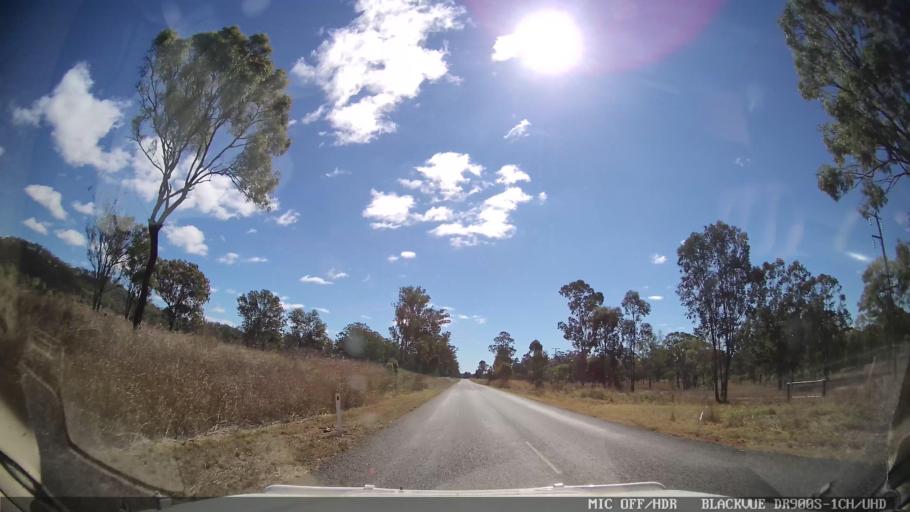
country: AU
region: Queensland
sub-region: Gladstone
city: Toolooa
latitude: -24.4446
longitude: 151.3422
